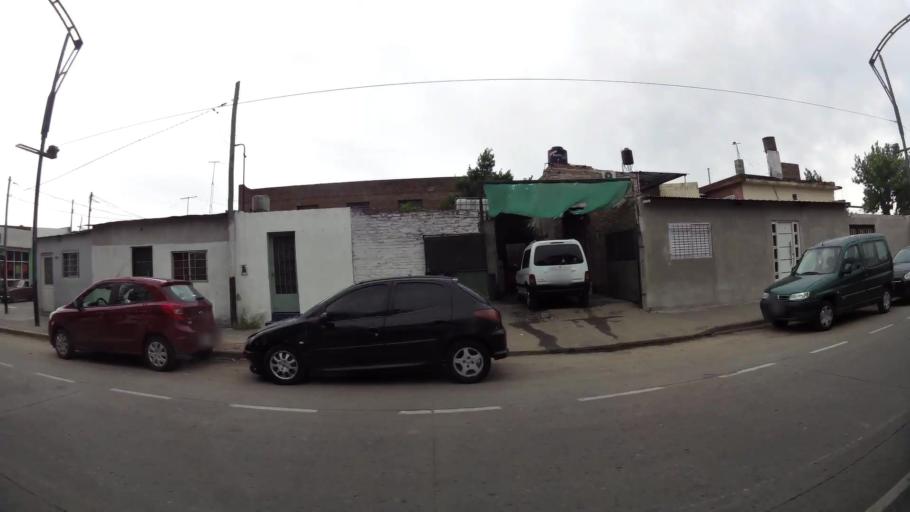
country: AR
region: Santa Fe
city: Gobernador Galvez
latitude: -32.9992
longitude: -60.6654
